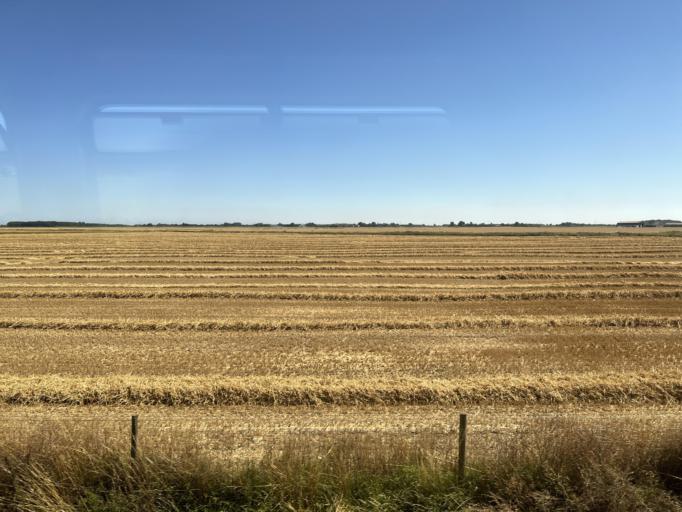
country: GB
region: England
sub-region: Lincolnshire
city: Spilsby
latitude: 53.1022
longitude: 0.1131
